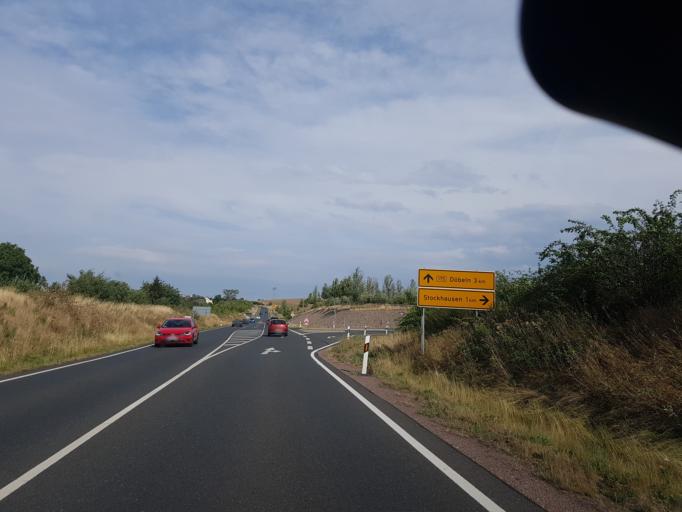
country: DE
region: Saxony
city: Dobeln
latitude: 51.1238
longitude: 13.0761
